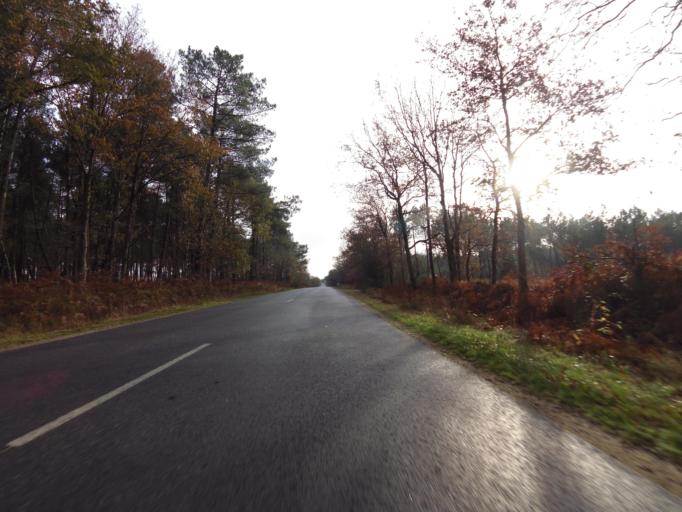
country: FR
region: Brittany
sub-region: Departement du Morbihan
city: Saint-Martin-sur-Oust
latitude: 47.7241
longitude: -2.2632
